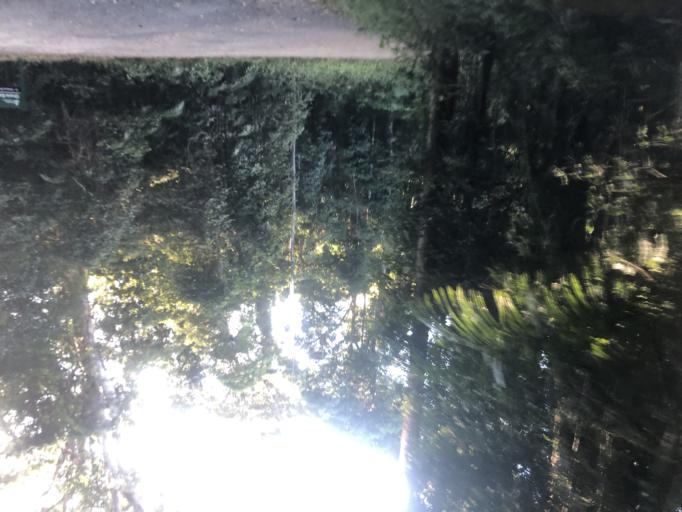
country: AU
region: New South Wales
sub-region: Coffs Harbour
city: Coffs Harbour
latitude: -30.2401
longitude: 153.0957
